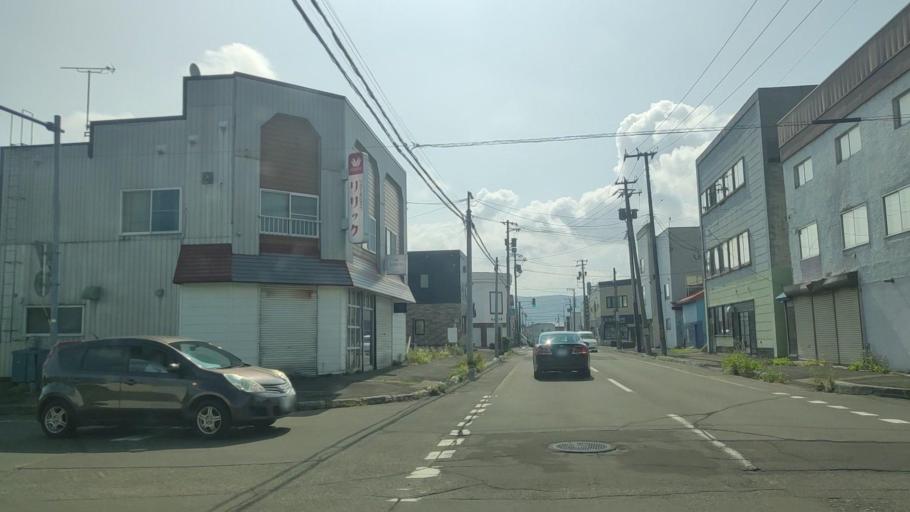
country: JP
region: Hokkaido
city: Shimo-furano
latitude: 43.3445
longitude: 142.3885
